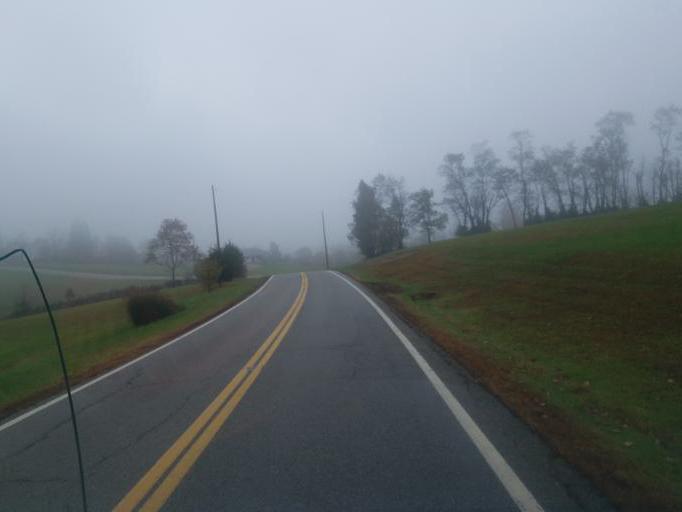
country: US
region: Ohio
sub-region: Morgan County
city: McConnelsville
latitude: 39.5263
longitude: -81.7928
